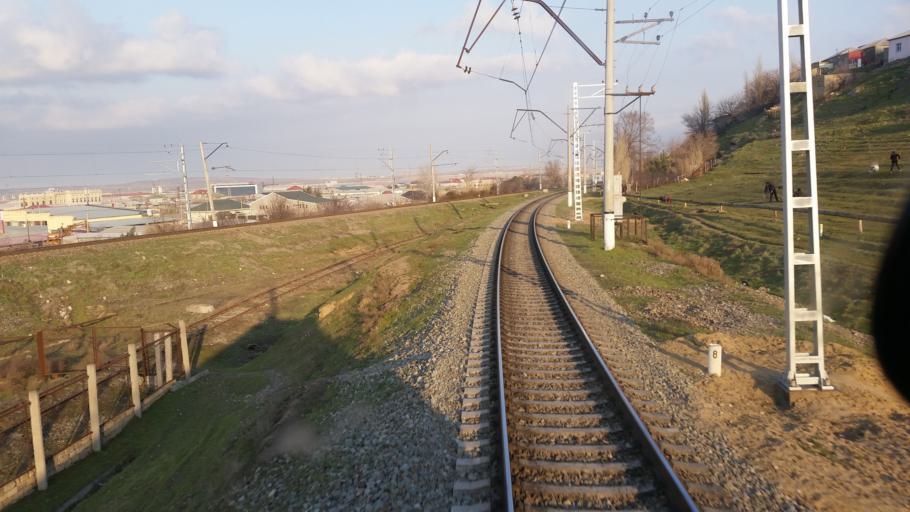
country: AZ
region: Baki
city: Binagadi
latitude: 40.4396
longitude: 49.8359
